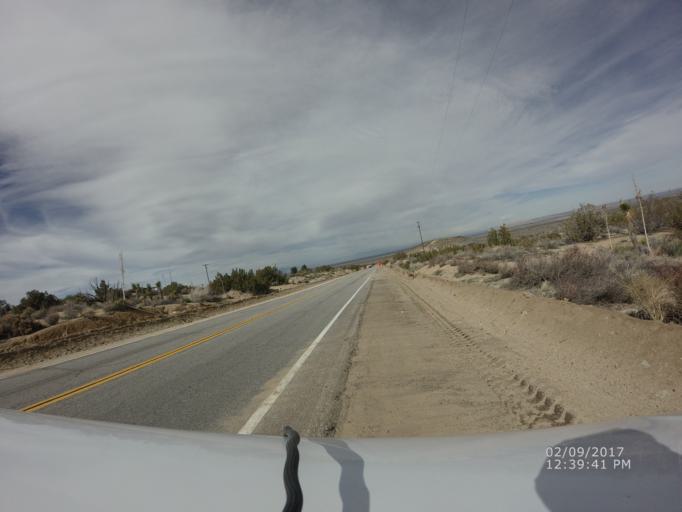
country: US
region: California
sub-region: Los Angeles County
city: Littlerock
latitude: 34.4827
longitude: -117.8672
